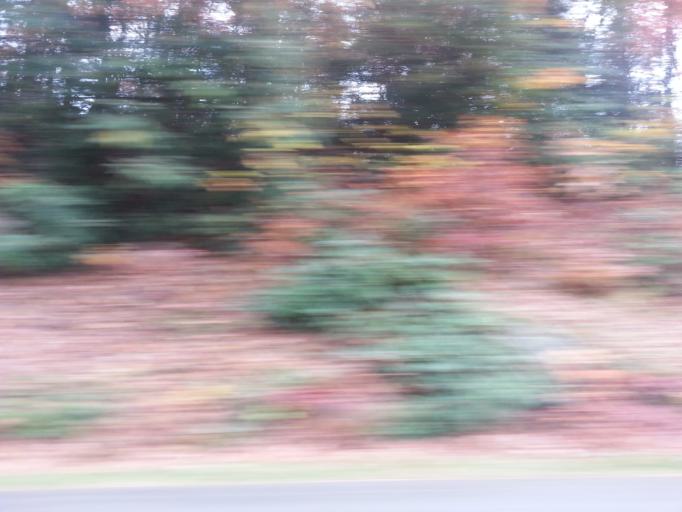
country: US
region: North Carolina
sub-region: Ashe County
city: Jefferson
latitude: 36.3231
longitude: -81.3684
